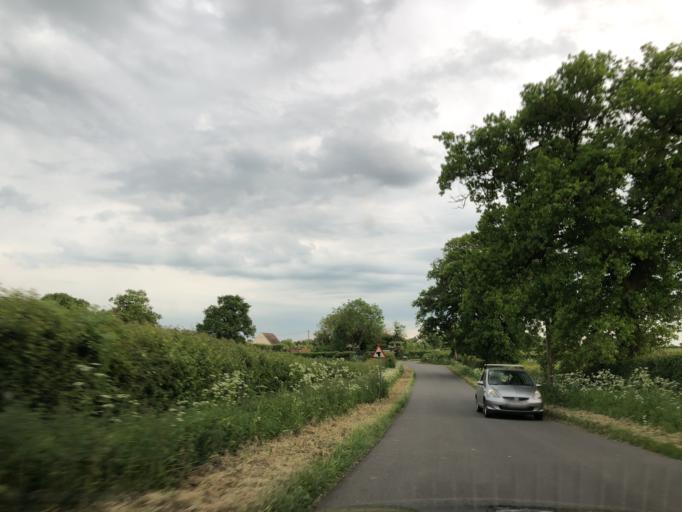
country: GB
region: England
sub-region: Warwickshire
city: Warwick
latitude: 52.2913
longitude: -1.6291
